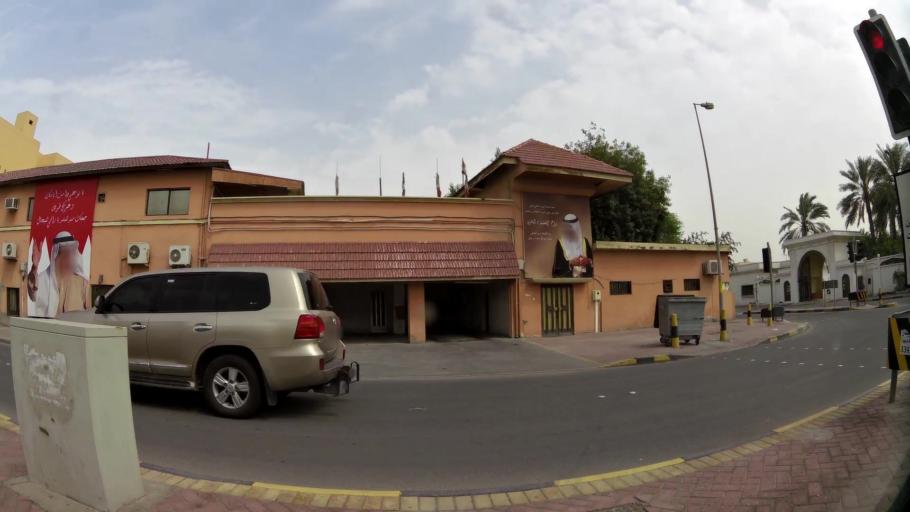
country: BH
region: Northern
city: Ar Rifa'
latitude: 26.1280
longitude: 50.5411
